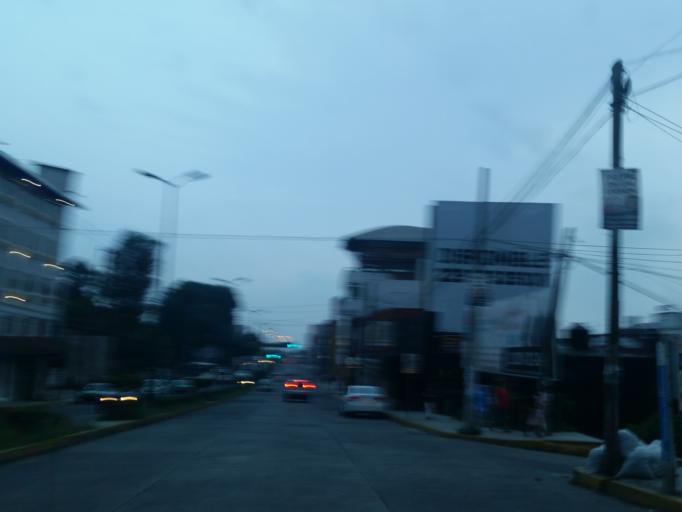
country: MX
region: Veracruz
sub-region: Xalapa
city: Xalapa de Enriquez
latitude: 19.5254
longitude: -96.9053
